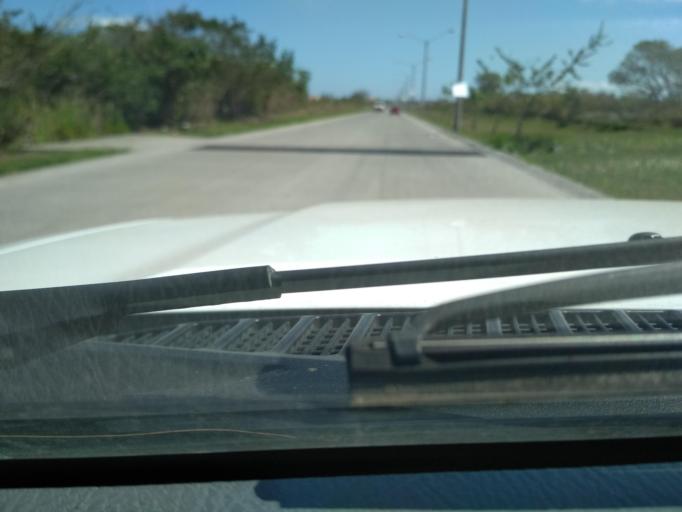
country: MX
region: Veracruz
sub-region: Veracruz
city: Las Amapolas
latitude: 19.1342
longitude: -96.2141
